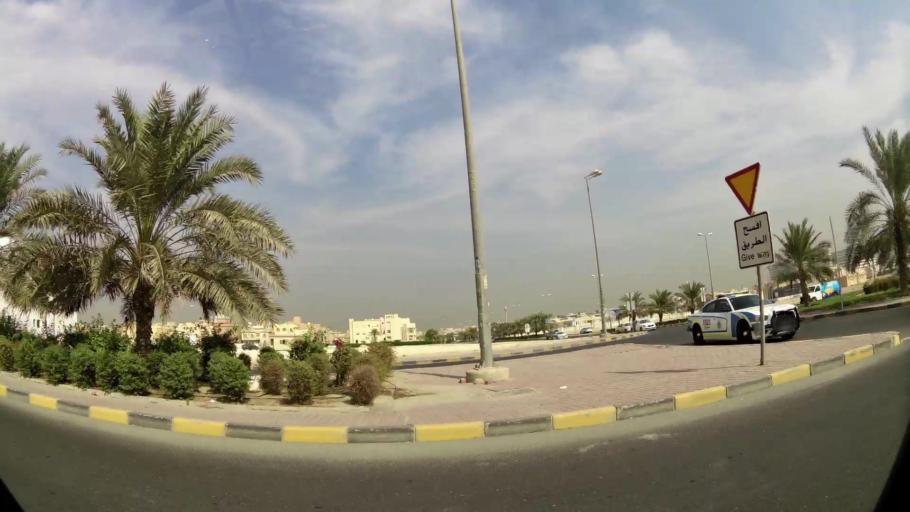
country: KW
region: Al Farwaniyah
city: Janub as Surrah
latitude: 29.2716
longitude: 48.0067
